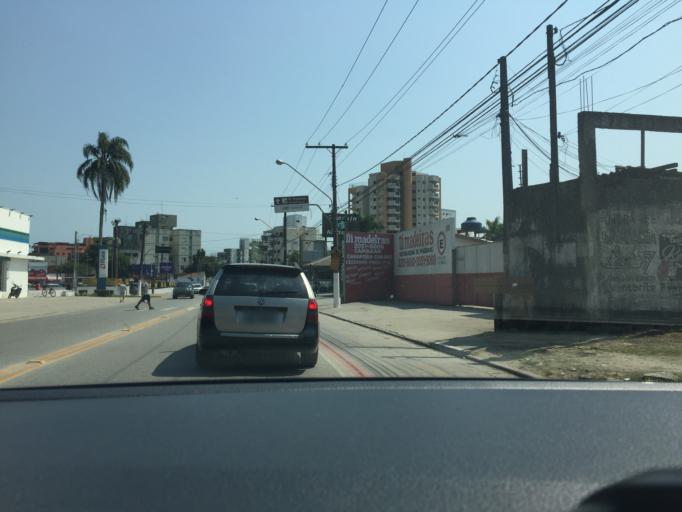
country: BR
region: Sao Paulo
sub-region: Guaruja
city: Guaruja
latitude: -23.9843
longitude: -46.2007
